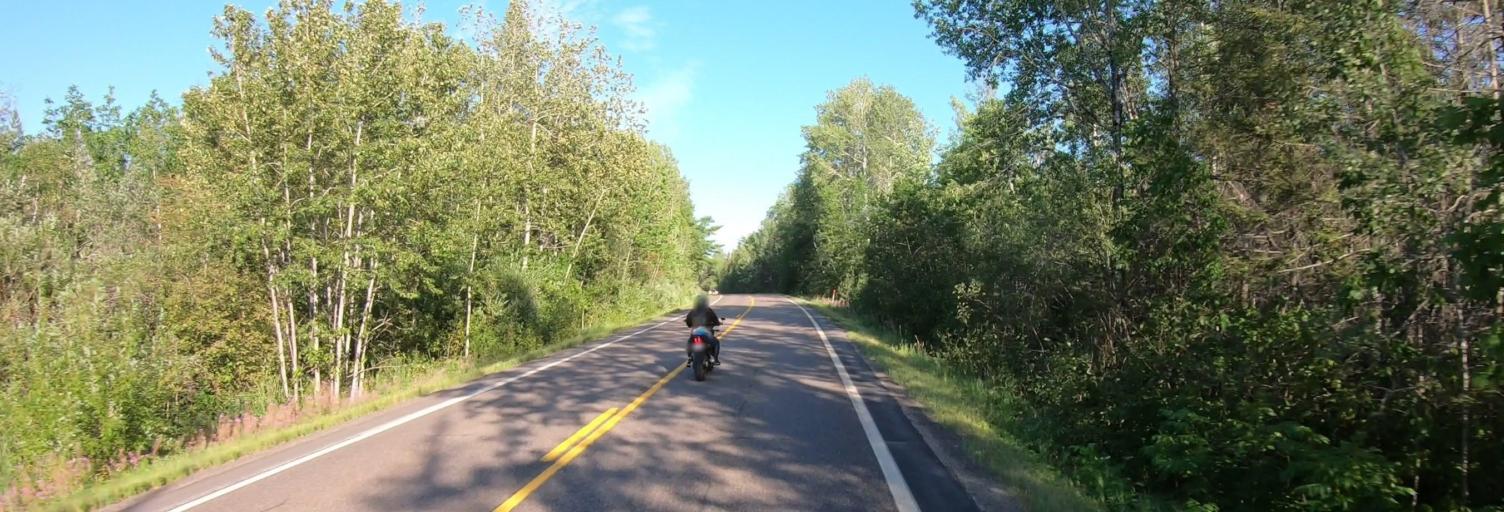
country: US
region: Minnesota
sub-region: Saint Louis County
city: Ely
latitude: 47.9579
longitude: -91.6187
